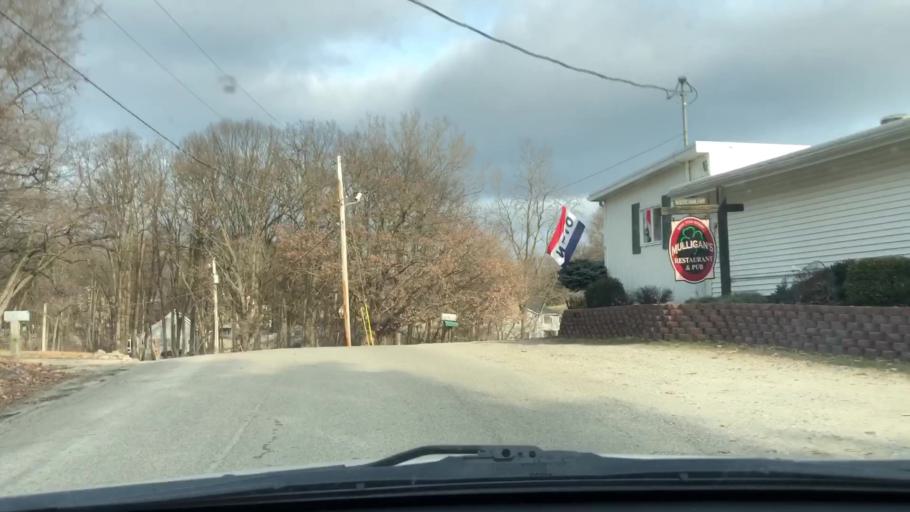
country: US
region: Indiana
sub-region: Steuben County
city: Angola
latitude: 41.6804
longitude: -85.0177
